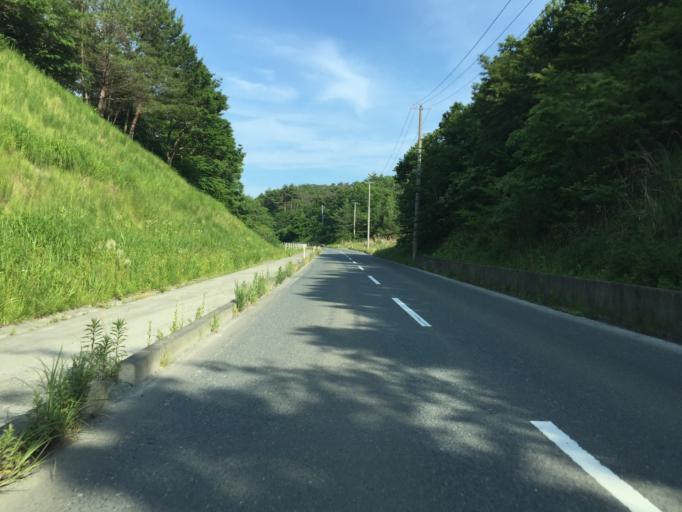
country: JP
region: Fukushima
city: Namie
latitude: 37.6692
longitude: 140.9699
